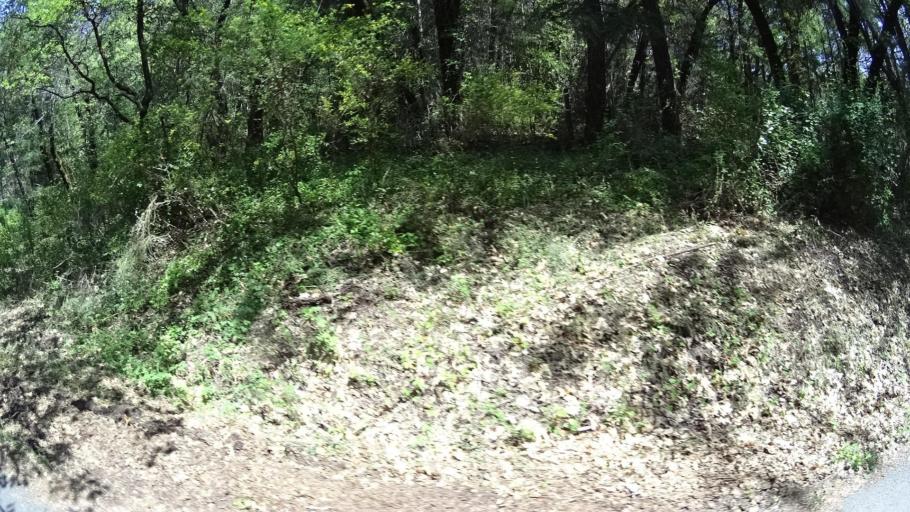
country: US
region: California
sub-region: Humboldt County
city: Redway
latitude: 40.2492
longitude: -123.6233
